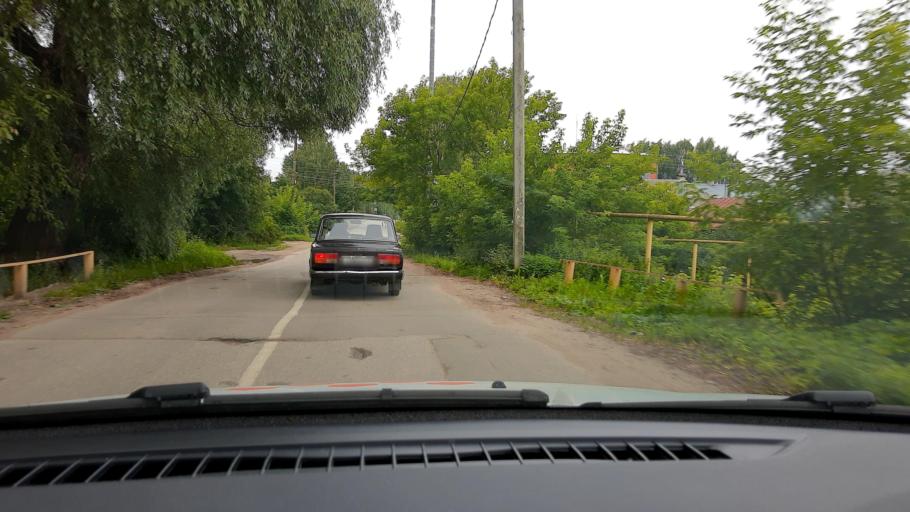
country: RU
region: Nizjnij Novgorod
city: Bogorodsk
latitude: 56.0948
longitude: 43.5134
